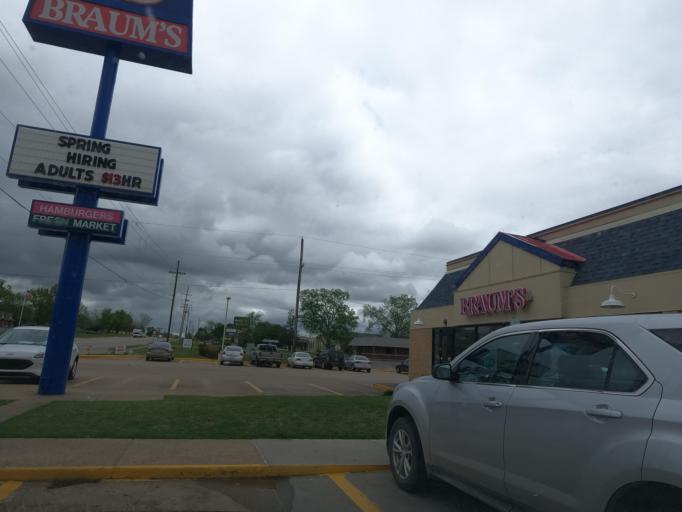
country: US
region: Kansas
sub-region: Labette County
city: Parsons
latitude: 37.3403
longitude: -95.2410
